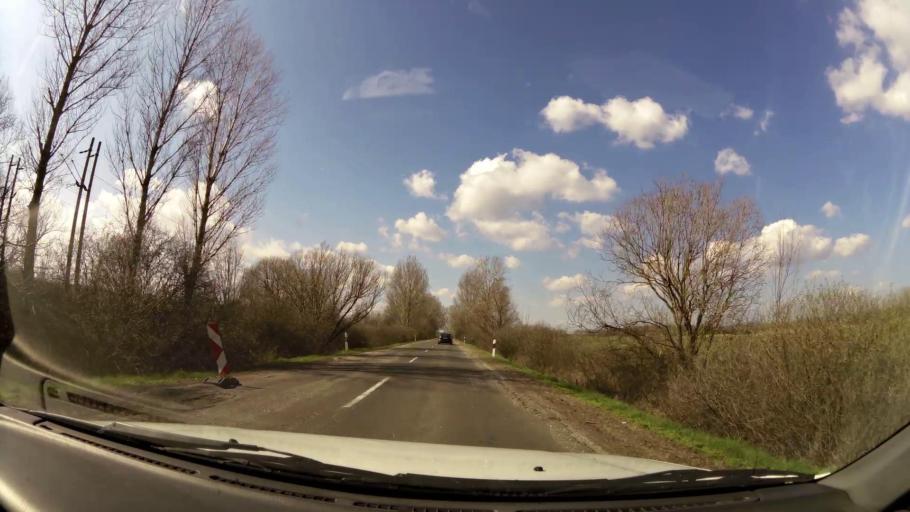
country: HU
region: Pest
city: Nagykata
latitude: 47.3831
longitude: 19.7826
